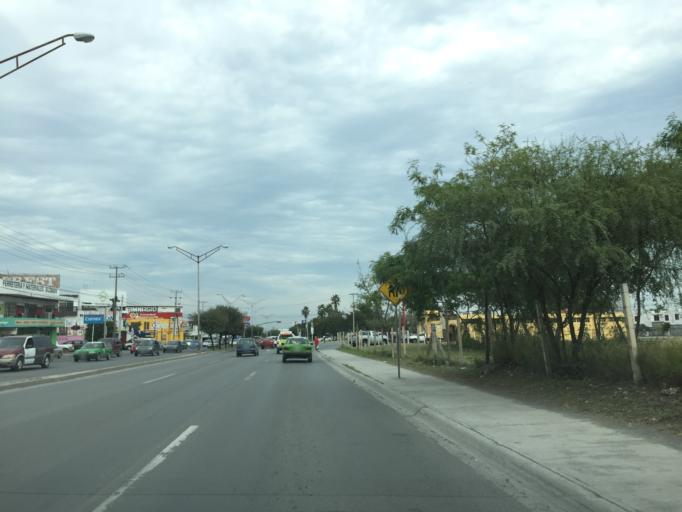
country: MX
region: Nuevo Leon
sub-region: Juarez
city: Jardines de la Silla (Jardines)
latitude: 25.6513
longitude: -100.1867
